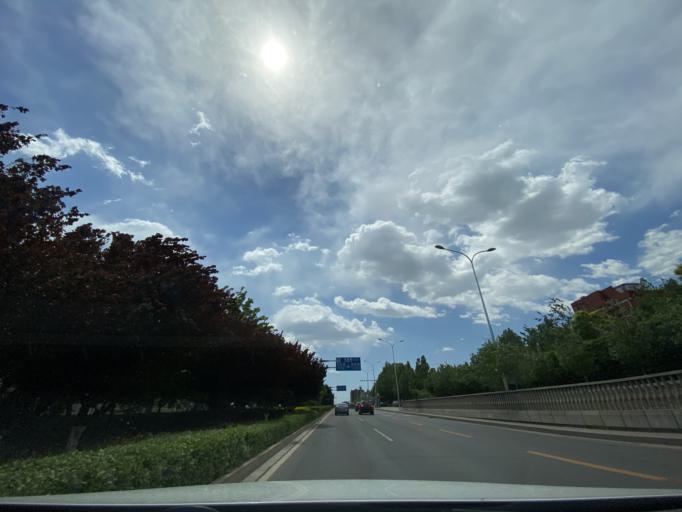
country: CN
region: Beijing
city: Sijiqing
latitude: 39.9308
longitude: 116.2468
